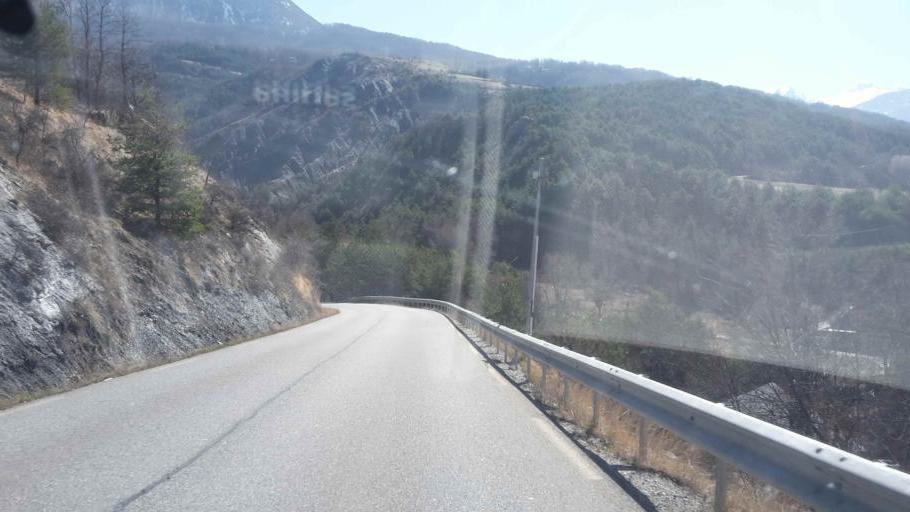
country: FR
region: Provence-Alpes-Cote d'Azur
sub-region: Departement des Hautes-Alpes
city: Embrun
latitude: 44.5665
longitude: 6.5215
